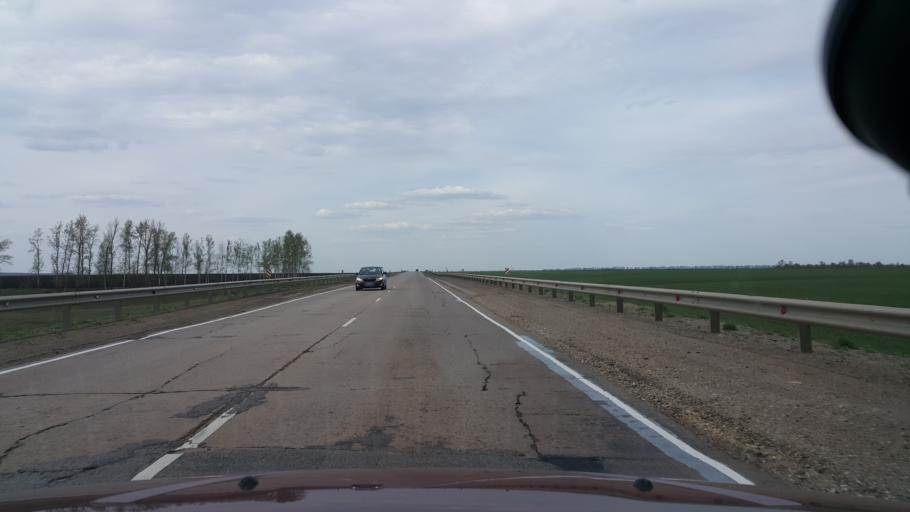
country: RU
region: Tambov
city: Pokrovo-Prigorodnoye
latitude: 52.6144
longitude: 41.3434
